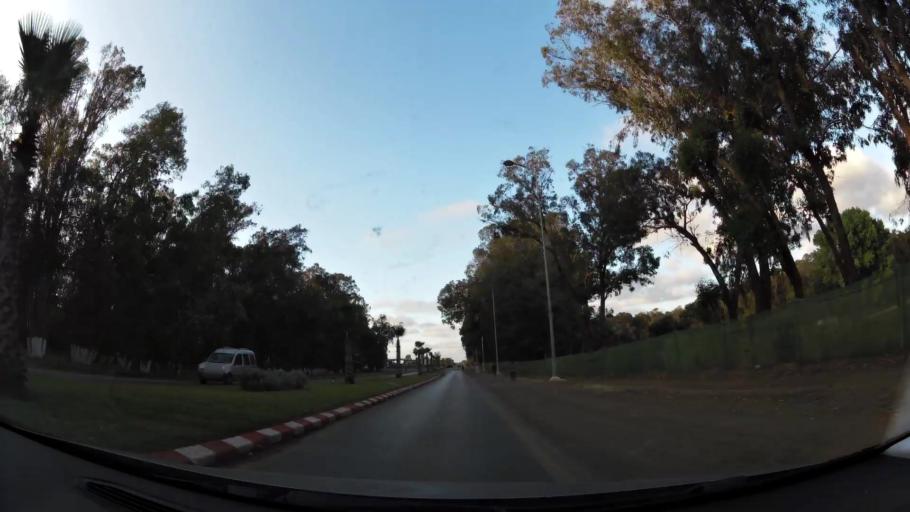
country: MA
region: Gharb-Chrarda-Beni Hssen
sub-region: Kenitra Province
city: Kenitra
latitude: 34.2017
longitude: -6.6774
